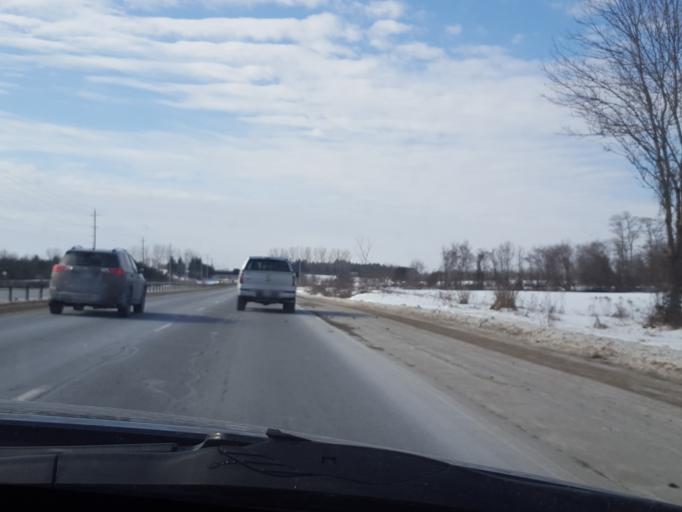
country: CA
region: Ontario
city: Barrie
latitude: 44.4709
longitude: -79.5544
